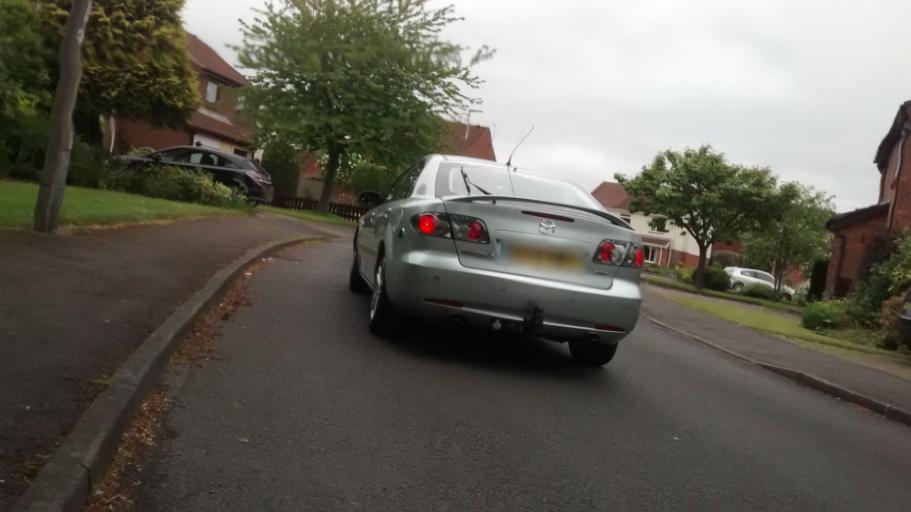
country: GB
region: England
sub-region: County Durham
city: Pittington
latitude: 54.7897
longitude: -1.4922
